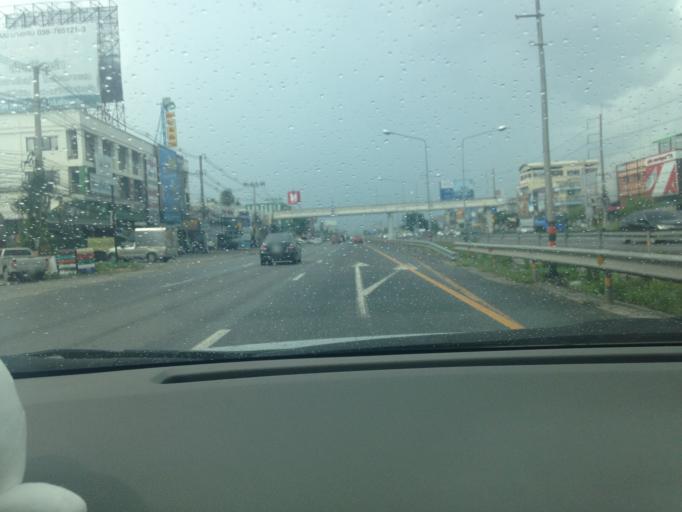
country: TH
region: Chon Buri
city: Chon Buri
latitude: 13.2972
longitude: 100.9461
